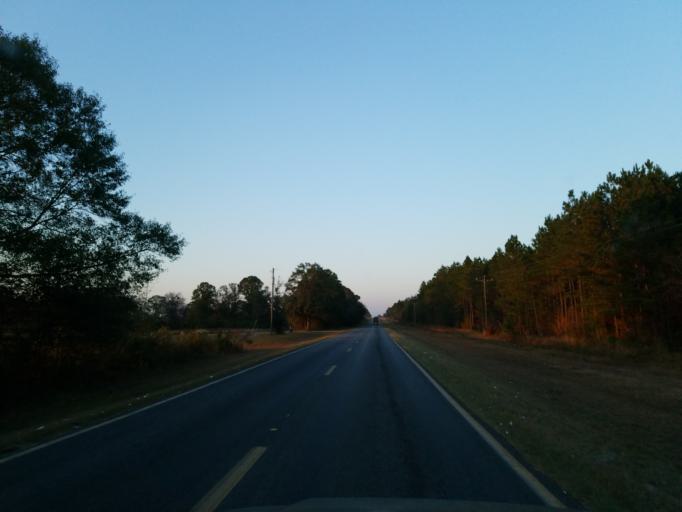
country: US
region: Georgia
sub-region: Ben Hill County
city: Fitzgerald
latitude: 31.6980
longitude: -83.3852
